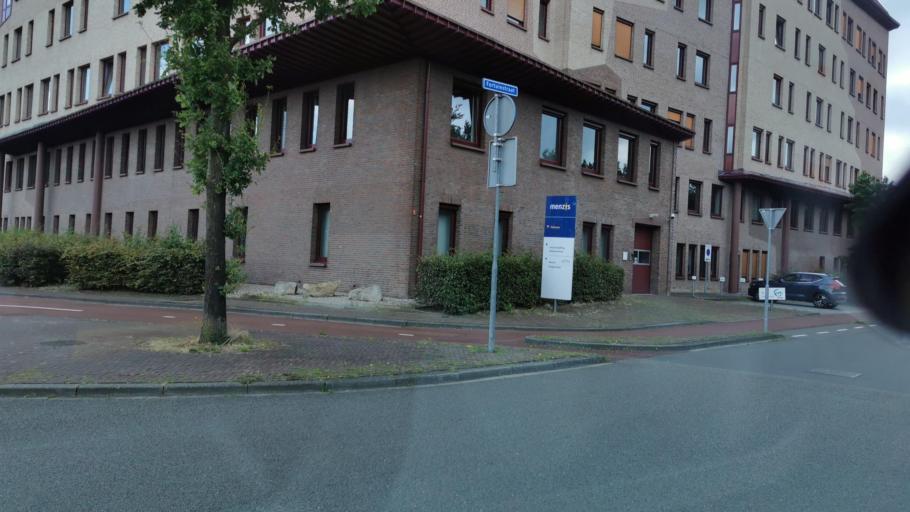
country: NL
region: Overijssel
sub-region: Gemeente Enschede
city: Enschede
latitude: 52.2243
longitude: 6.8854
